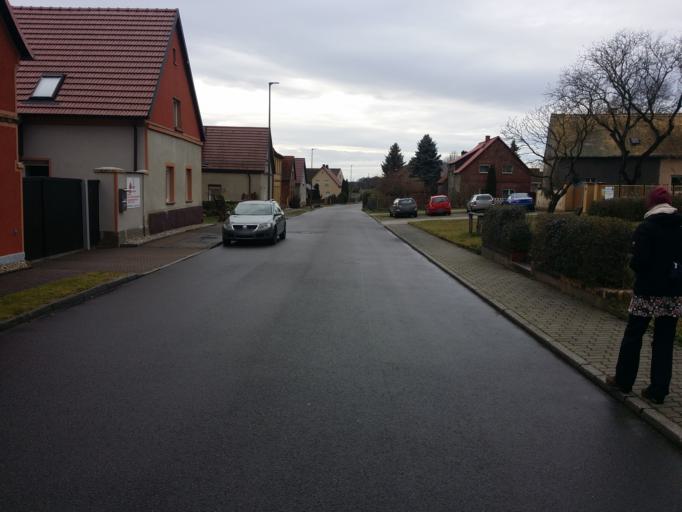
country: DE
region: Saxony
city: Kossa
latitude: 51.5922
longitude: 12.6779
